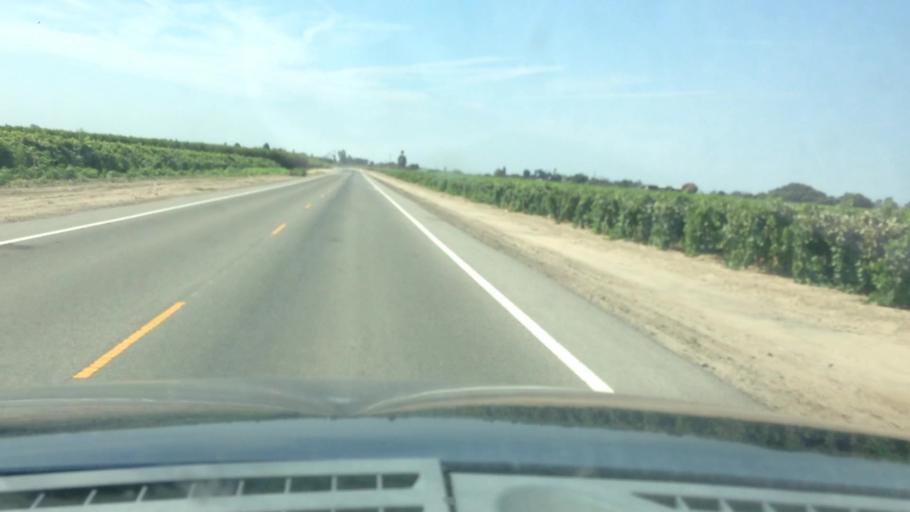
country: US
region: California
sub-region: Fresno County
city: Parlier
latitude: 36.5816
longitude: -119.5573
